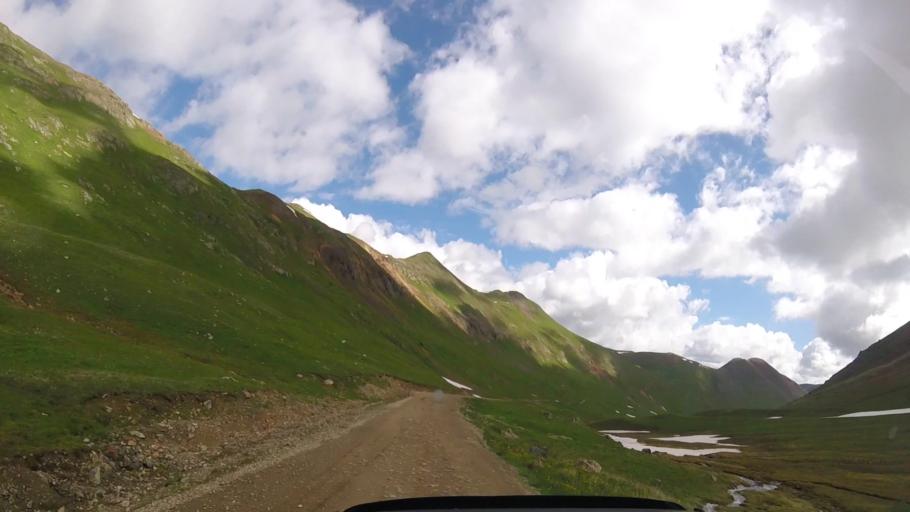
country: US
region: Colorado
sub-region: Ouray County
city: Ouray
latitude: 37.9198
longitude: -107.6126
